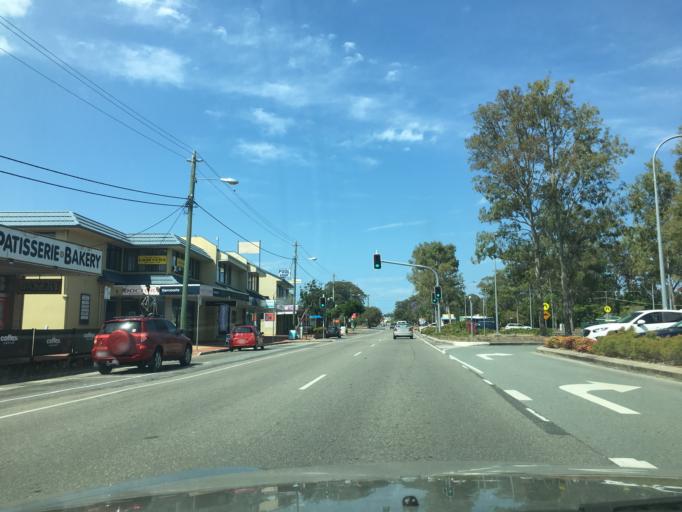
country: AU
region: Queensland
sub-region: Moreton Bay
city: Bongaree
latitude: -27.0659
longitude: 153.1506
